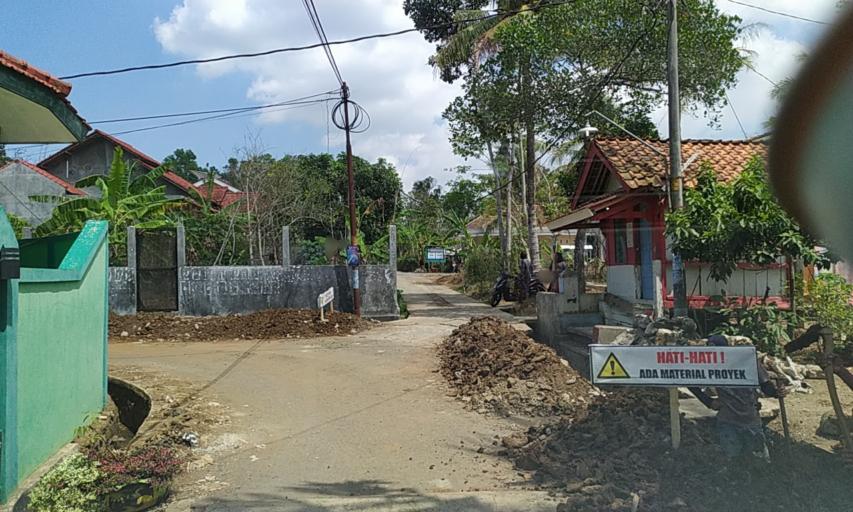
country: ID
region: Central Java
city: Kroya
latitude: -7.6365
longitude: 109.2396
